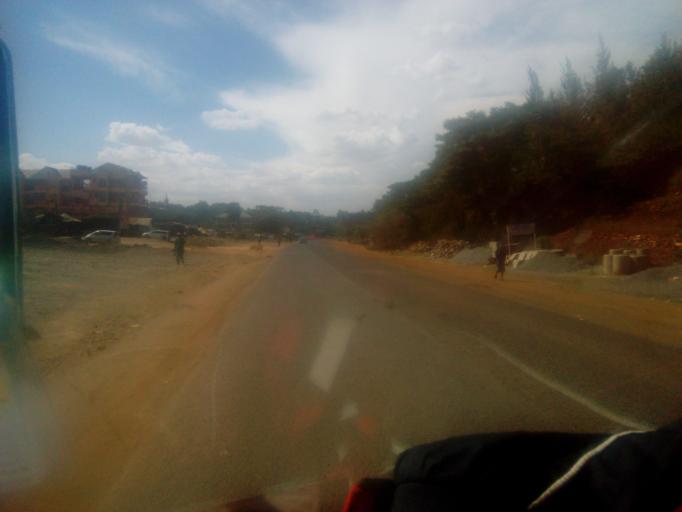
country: KE
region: Kiambu
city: Kikuyu
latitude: -1.2781
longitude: 36.6877
